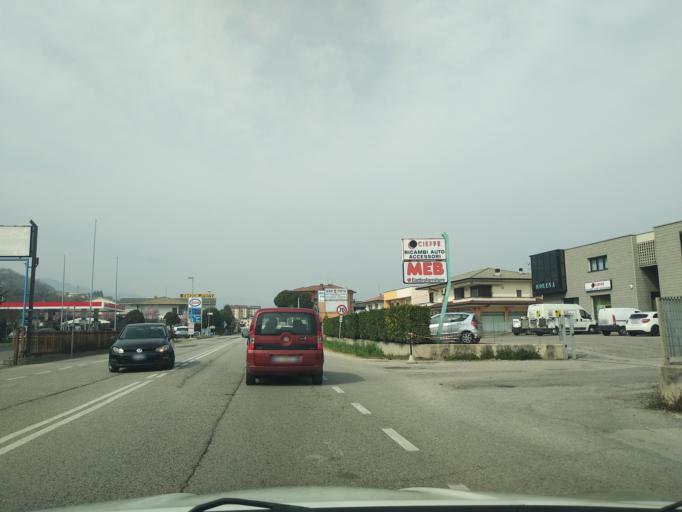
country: IT
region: Veneto
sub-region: Provincia di Vicenza
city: Arzignano
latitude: 45.5147
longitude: 11.3407
